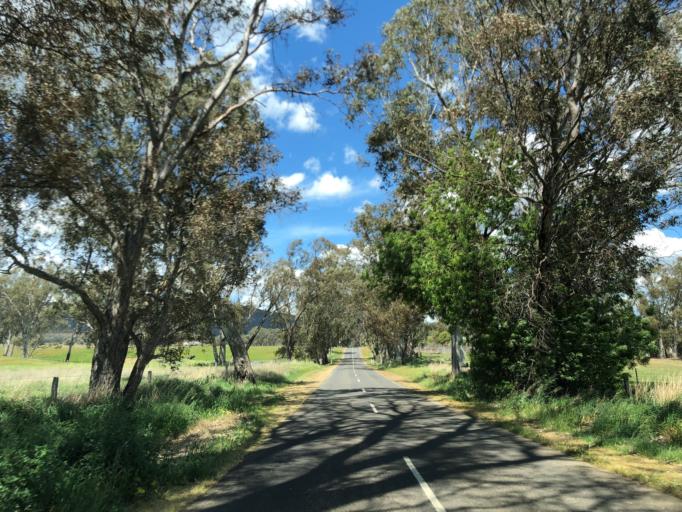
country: AU
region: Victoria
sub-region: Benalla
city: Benalla
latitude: -36.7343
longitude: 146.1116
